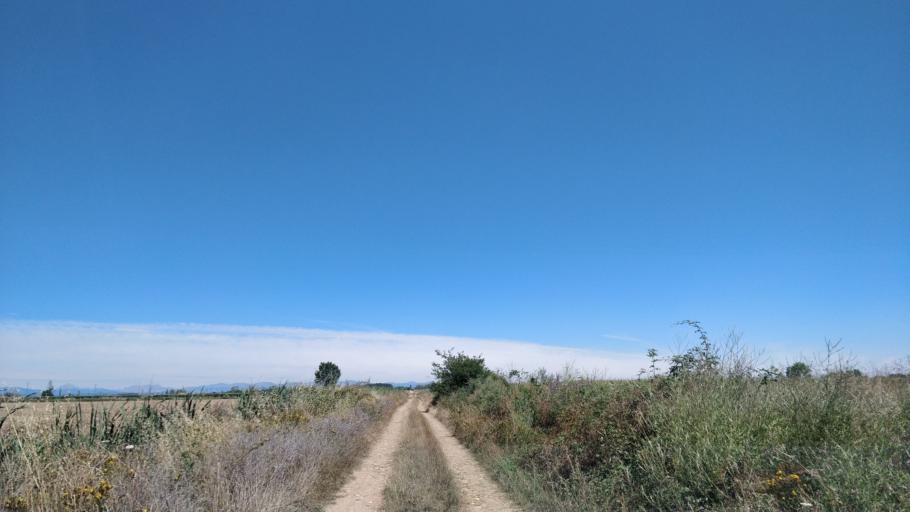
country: ES
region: Castille and Leon
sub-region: Provincia de Leon
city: Bustillo del Paramo
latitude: 42.4625
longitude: -5.8157
